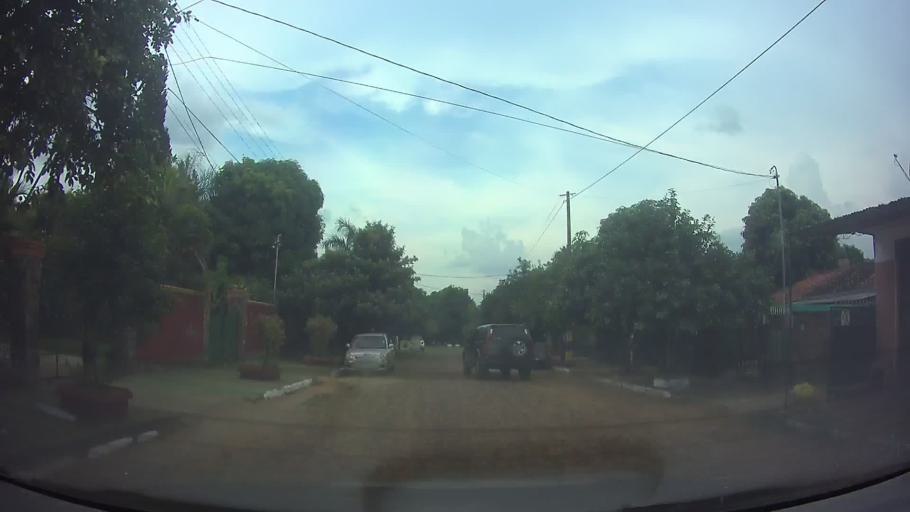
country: PY
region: Central
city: San Lorenzo
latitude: -25.2830
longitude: -57.4939
